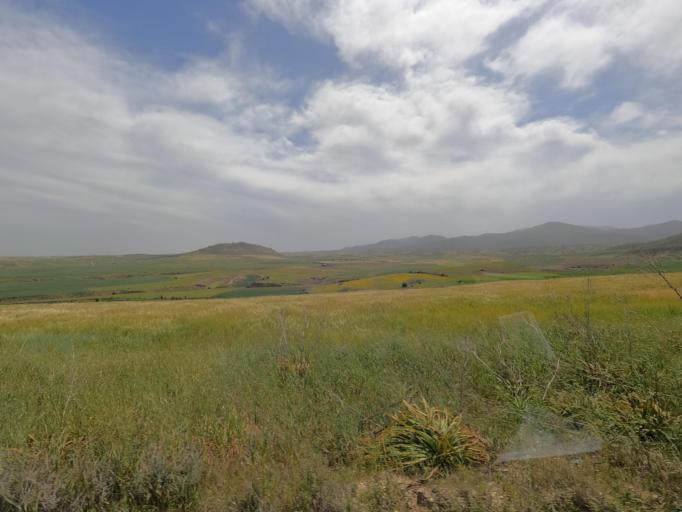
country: CY
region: Lefkosia
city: Lefka
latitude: 35.0980
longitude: 32.9364
